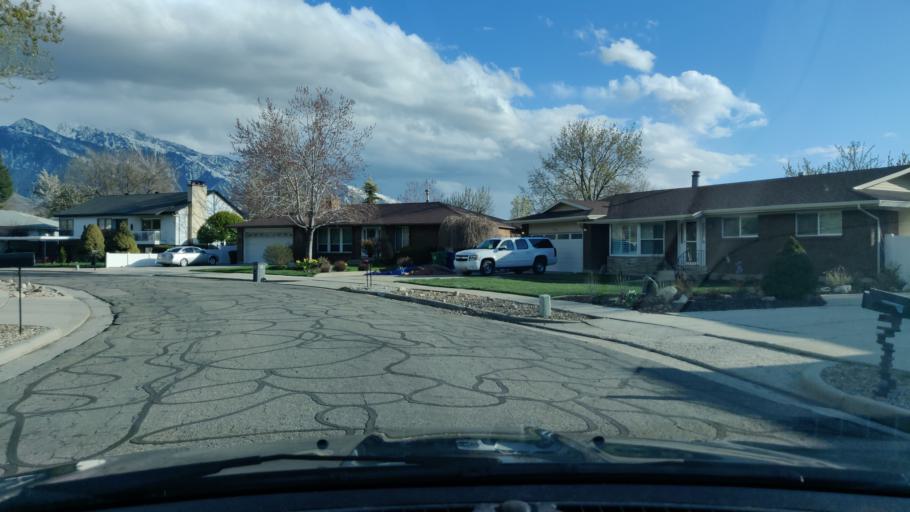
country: US
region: Utah
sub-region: Salt Lake County
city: Cottonwood Heights
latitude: 40.6210
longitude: -111.8168
